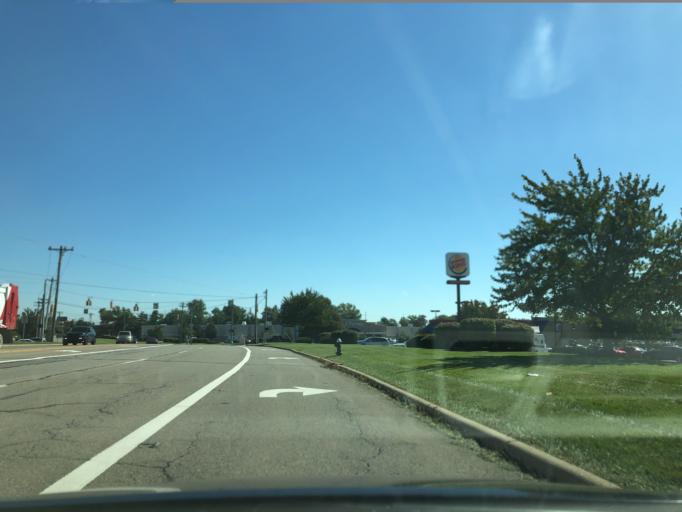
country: US
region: Ohio
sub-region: Hamilton County
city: Sixteen Mile Stand
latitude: 39.2916
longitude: -84.3063
